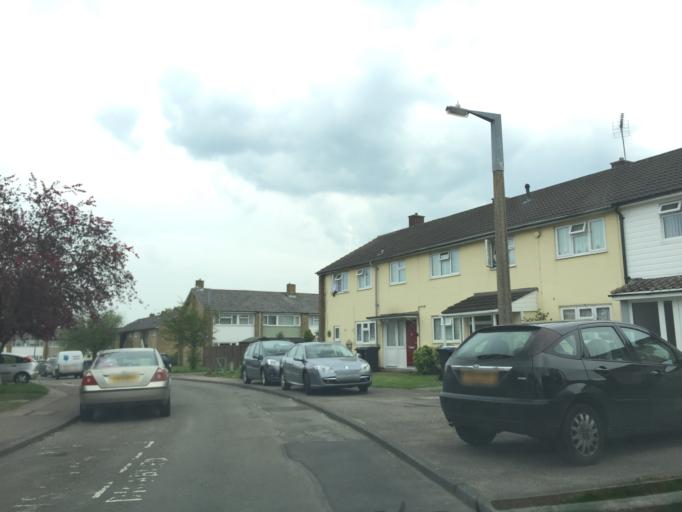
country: GB
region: England
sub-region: Essex
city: Harlow
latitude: 51.7600
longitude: 0.1222
